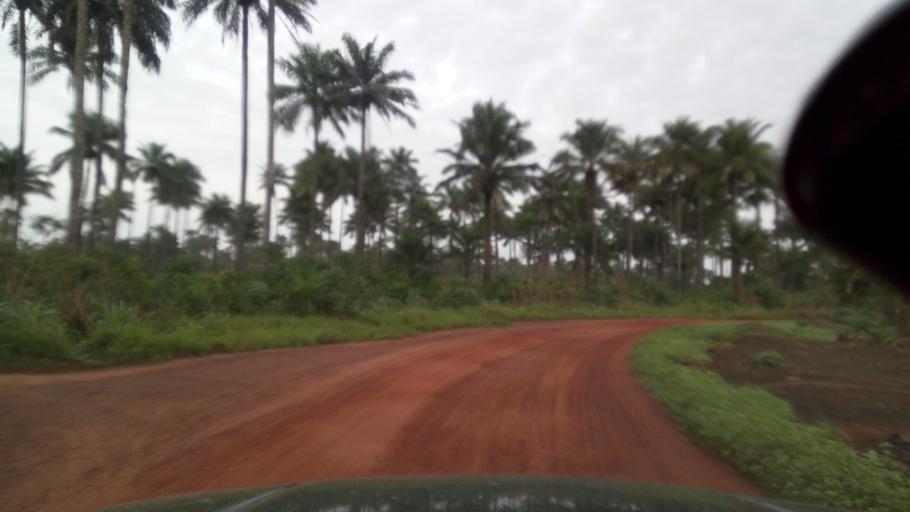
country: SL
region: Northern Province
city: Port Loko
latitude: 8.7233
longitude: -12.7947
